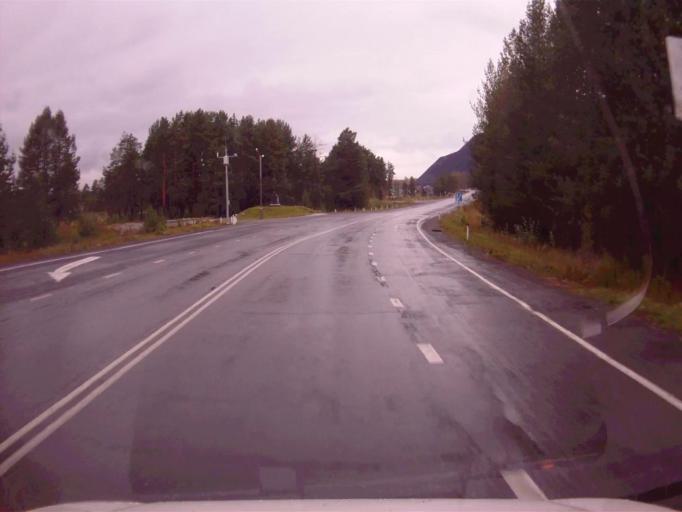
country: RU
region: Chelyabinsk
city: Verkhniy Ufaley
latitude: 56.0280
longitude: 60.2869
